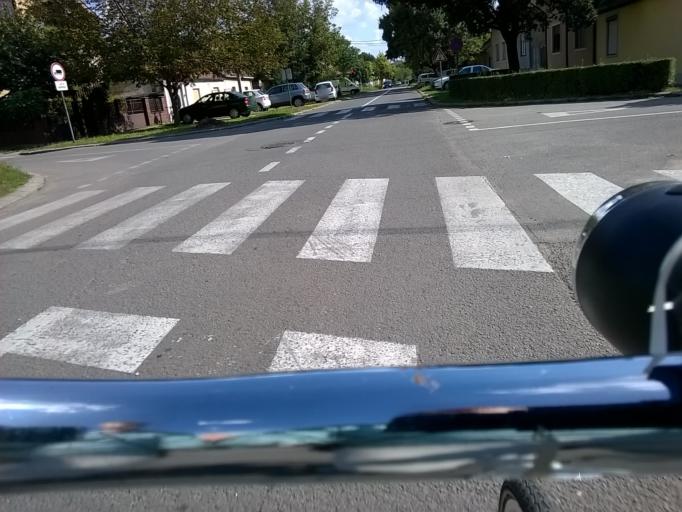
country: RS
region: Autonomna Pokrajina Vojvodina
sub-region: Juznobanatski Okrug
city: Pancevo
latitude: 44.8788
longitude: 20.6424
